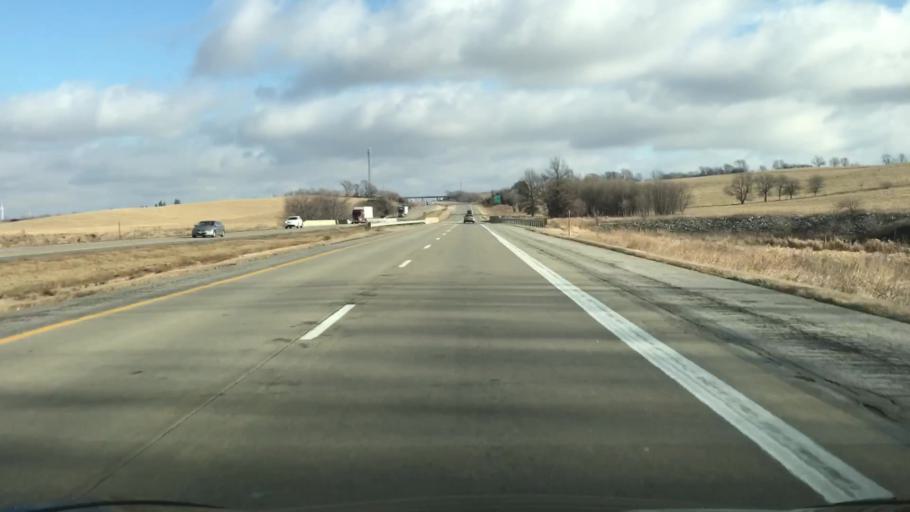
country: US
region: Iowa
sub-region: Cass County
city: Atlantic
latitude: 41.4963
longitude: -94.7909
